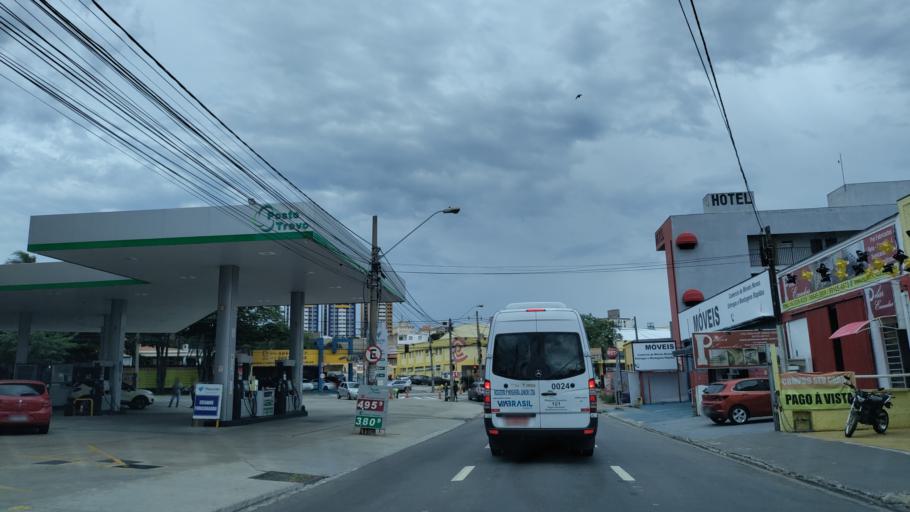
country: BR
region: Sao Paulo
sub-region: Sorocaba
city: Sorocaba
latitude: -23.4828
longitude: -47.4728
